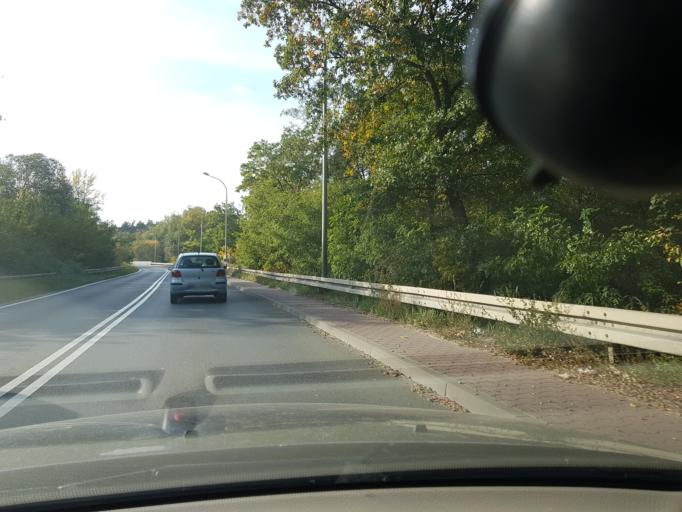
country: PL
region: Masovian Voivodeship
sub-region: Powiat otwocki
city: Otwock
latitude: 52.1064
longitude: 21.2313
